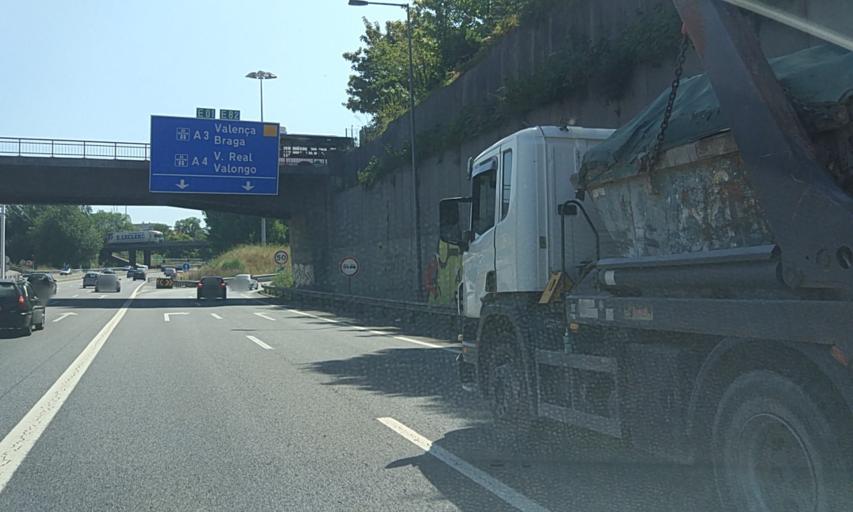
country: PT
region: Porto
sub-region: Porto
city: Porto
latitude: 41.1724
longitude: -8.5998
